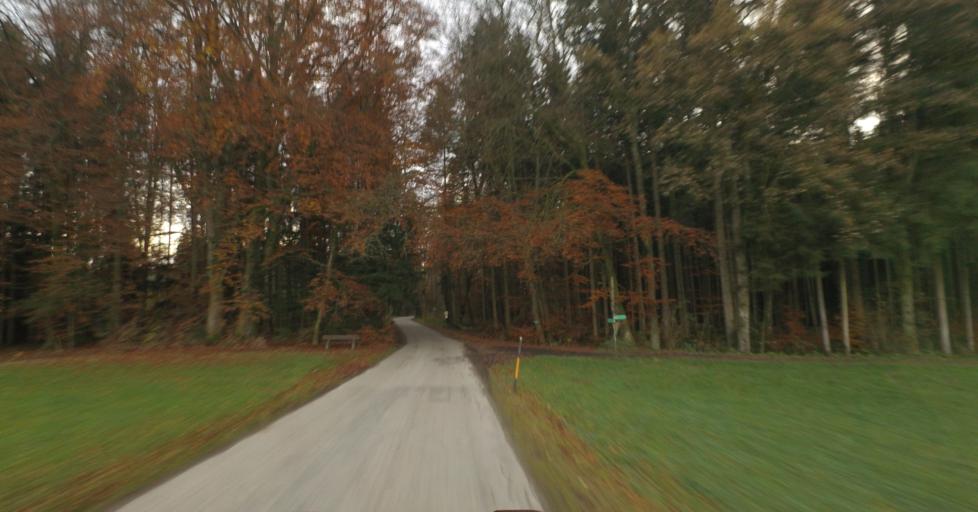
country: DE
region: Bavaria
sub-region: Upper Bavaria
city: Gstadt am Chiemsee
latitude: 47.9036
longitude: 12.4189
